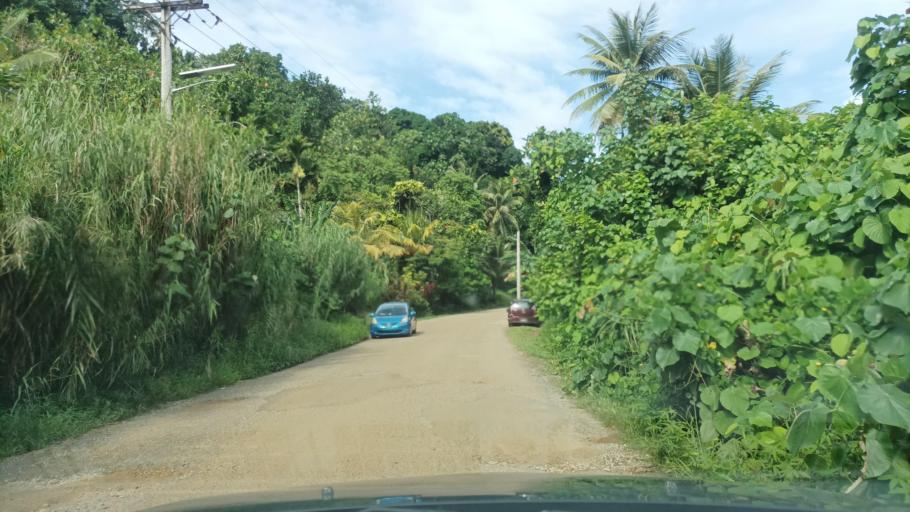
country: FM
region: Kosrae
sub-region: Lelu Municipality
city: Lelu
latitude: 5.3381
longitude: 163.0149
